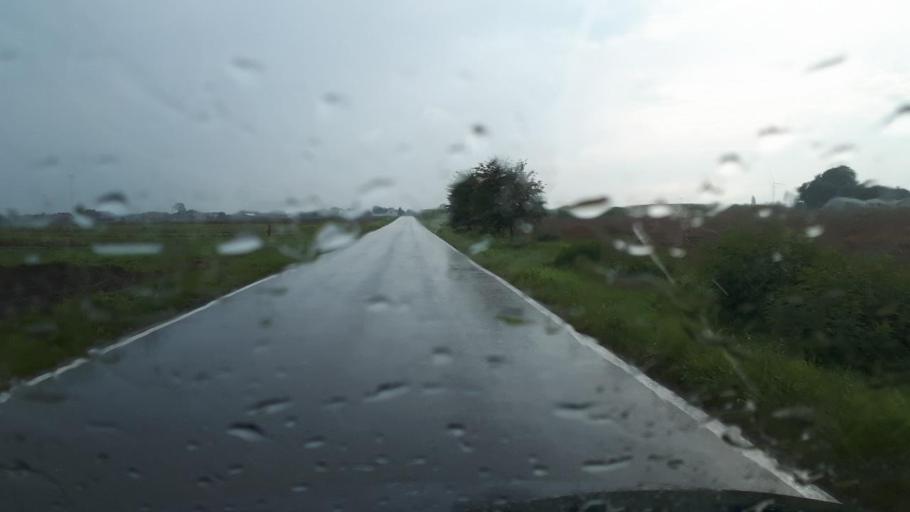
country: PL
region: Silesian Voivodeship
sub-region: Powiat gliwicki
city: Wielowies
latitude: 50.5191
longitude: 18.6302
